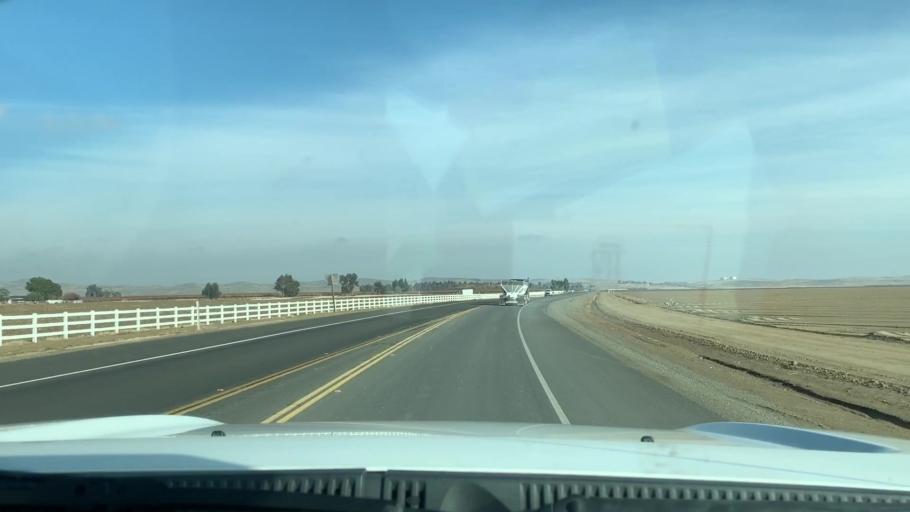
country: US
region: California
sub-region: Fresno County
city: Coalinga
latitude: 36.1814
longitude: -120.3524
